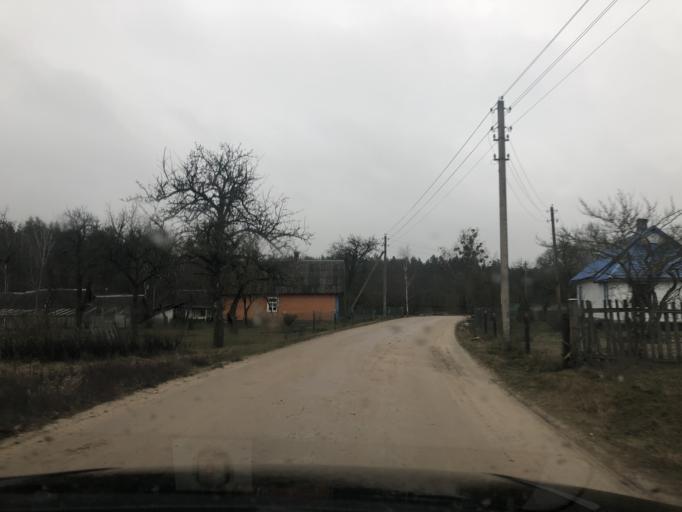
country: BY
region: Grodnenskaya
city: Skidal'
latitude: 53.8588
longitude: 24.2505
